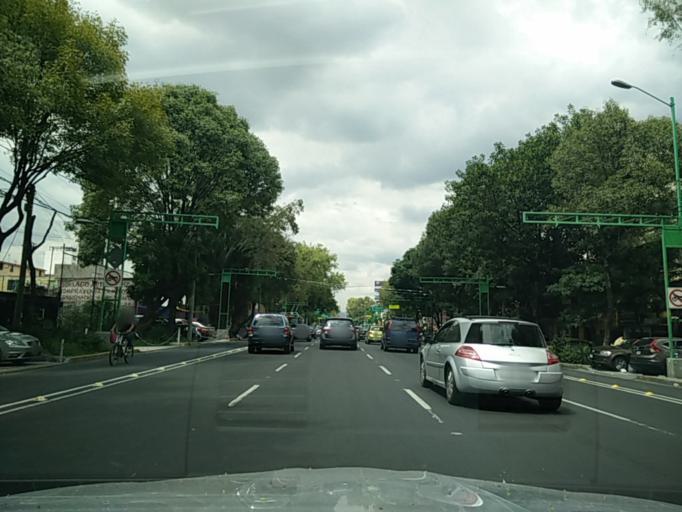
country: MX
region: Mexico City
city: Colonia Nativitas
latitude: 19.3846
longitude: -99.1473
